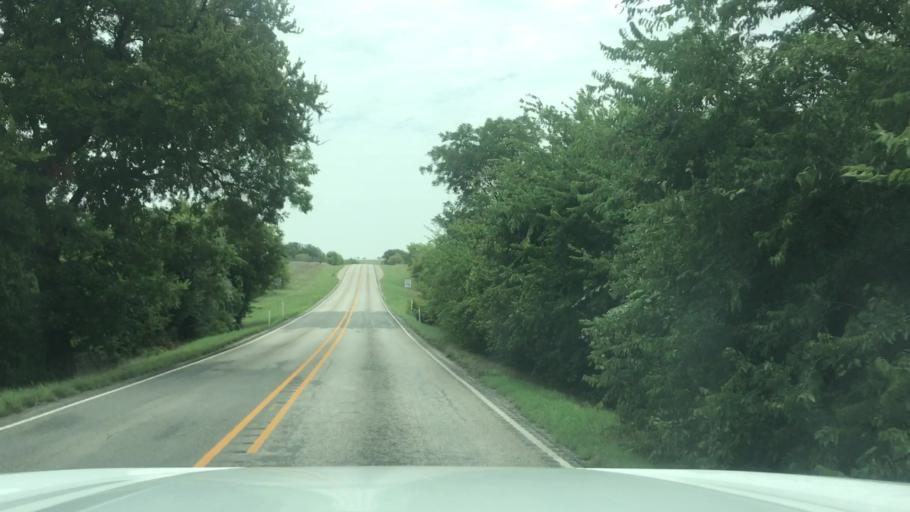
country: US
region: Texas
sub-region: Erath County
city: Dublin
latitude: 32.0578
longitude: -98.1967
